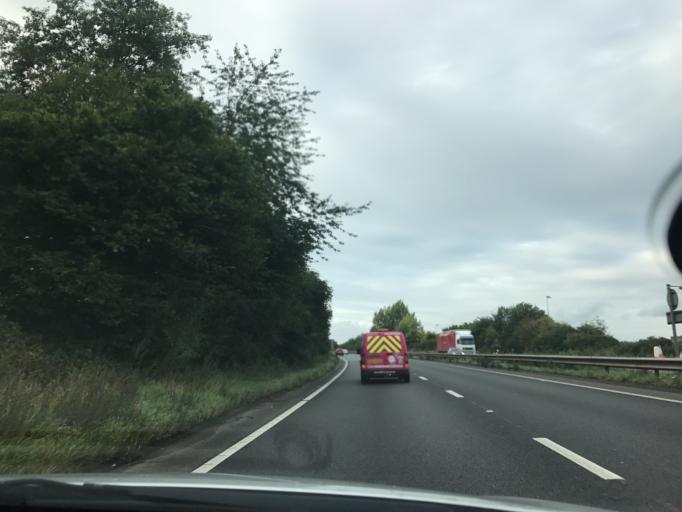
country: GB
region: England
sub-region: Cheshire West and Chester
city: Guilden Sutton
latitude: 53.2043
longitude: -2.8437
